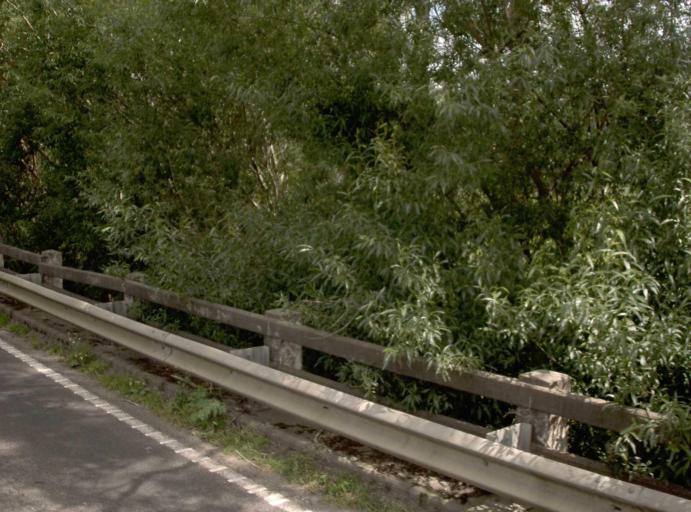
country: AU
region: Victoria
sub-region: Baw Baw
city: Warragul
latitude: -38.4452
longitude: 146.0109
